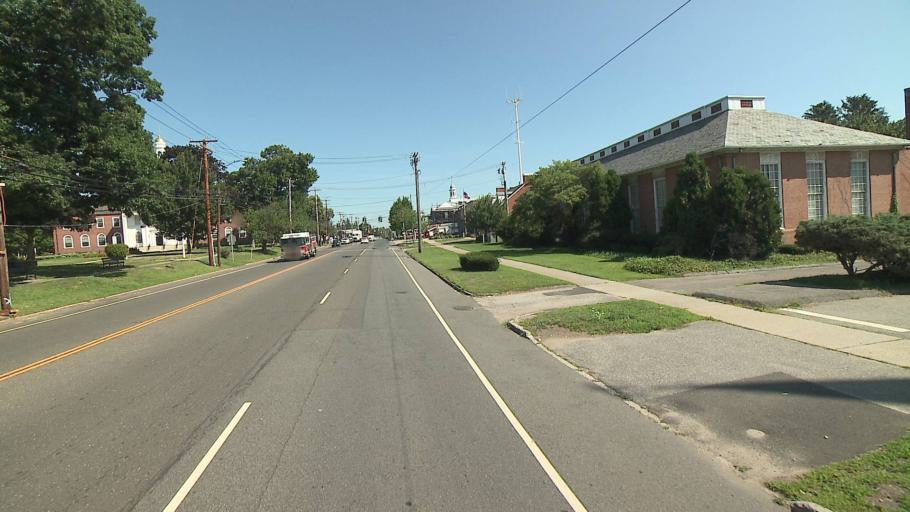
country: US
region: Connecticut
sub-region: Fairfield County
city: Stratford
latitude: 41.1966
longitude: -73.1319
